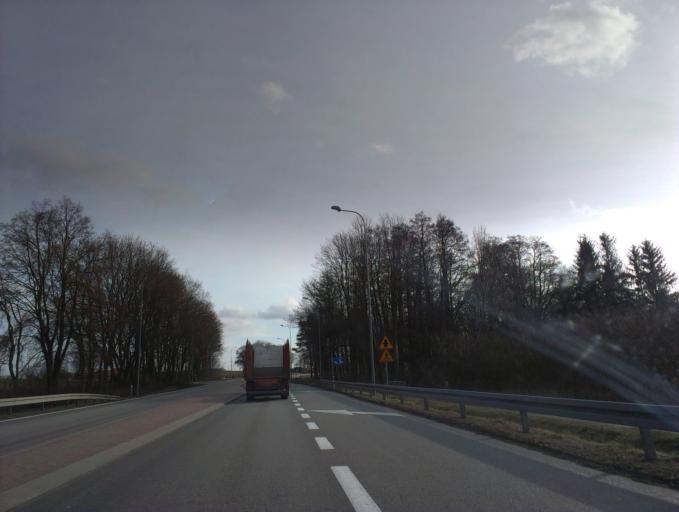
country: PL
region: Kujawsko-Pomorskie
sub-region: Powiat lipnowski
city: Lipno
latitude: 52.8728
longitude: 19.1506
